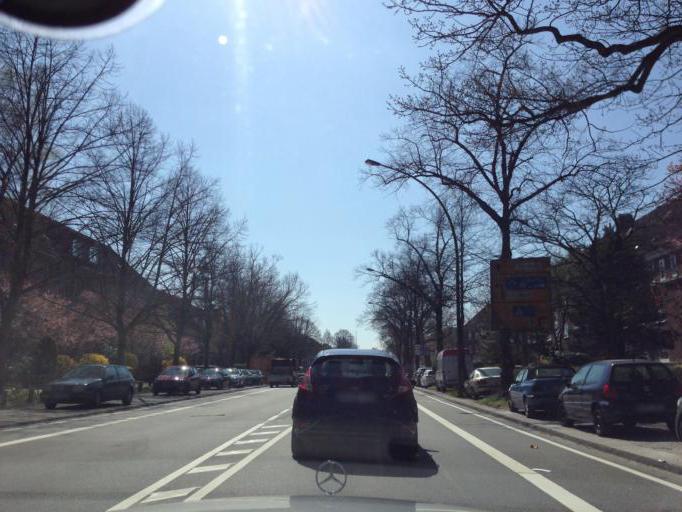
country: DE
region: Hamburg
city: Fuhlsbuettel
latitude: 53.6254
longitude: 10.0122
